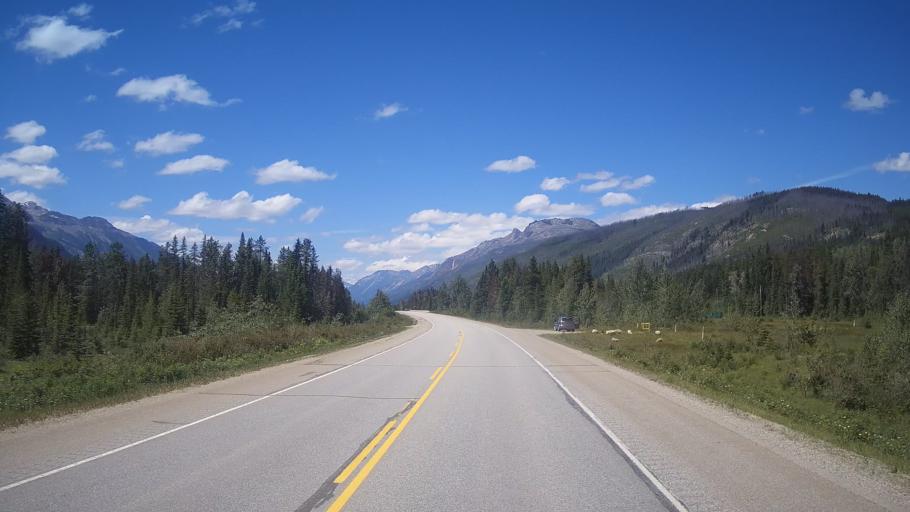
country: CA
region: Alberta
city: Jasper Park Lodge
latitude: 52.9174
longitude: -118.7965
